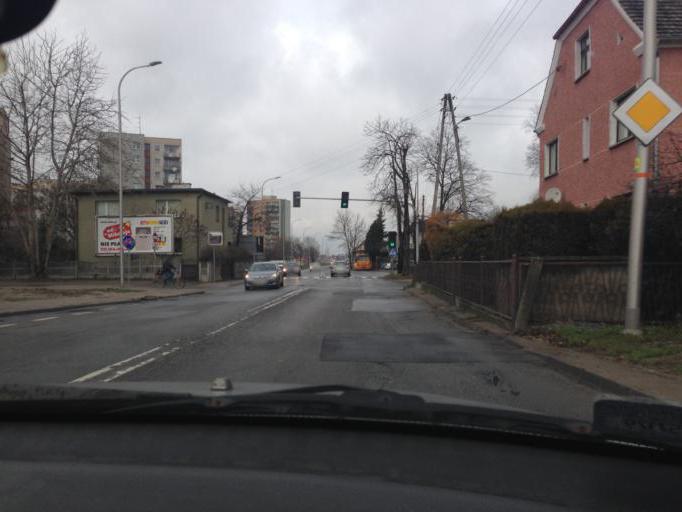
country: PL
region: Opole Voivodeship
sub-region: Powiat opolski
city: Opole
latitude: 50.6825
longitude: 17.9549
